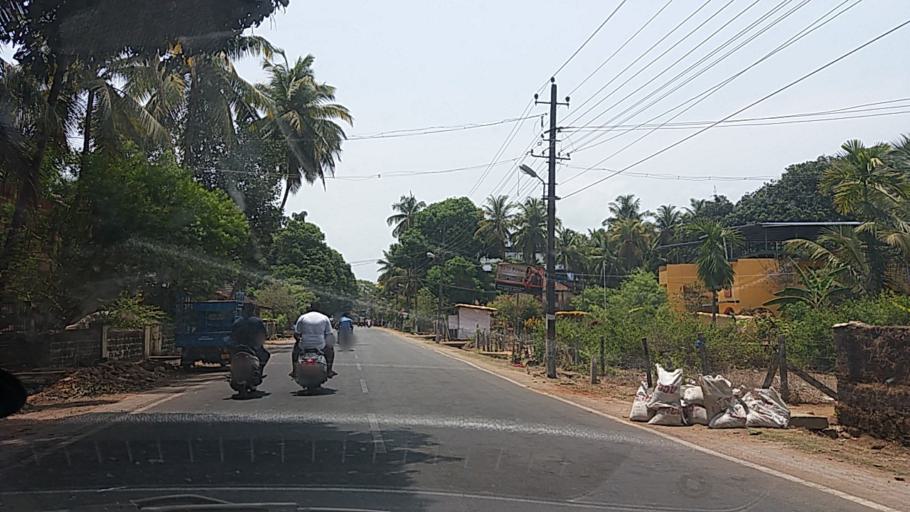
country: IN
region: Karnataka
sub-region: Uttar Kannada
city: Karwar
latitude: 14.8104
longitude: 74.1390
